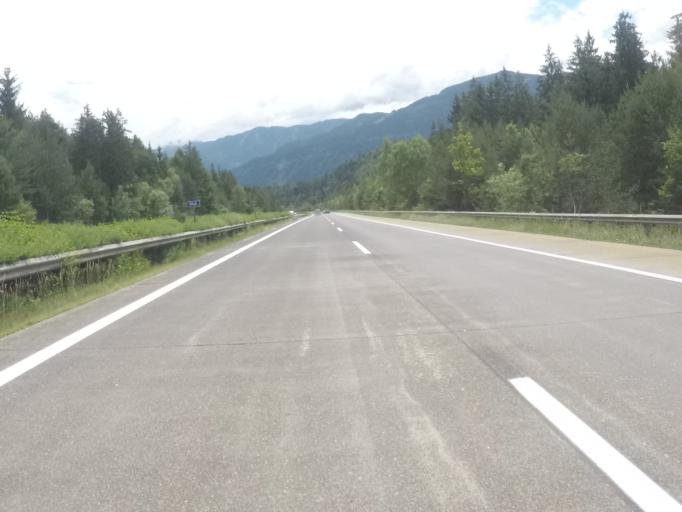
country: AT
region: Carinthia
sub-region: Politischer Bezirk Villach Land
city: Arnoldstein
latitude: 46.5627
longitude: 13.7414
